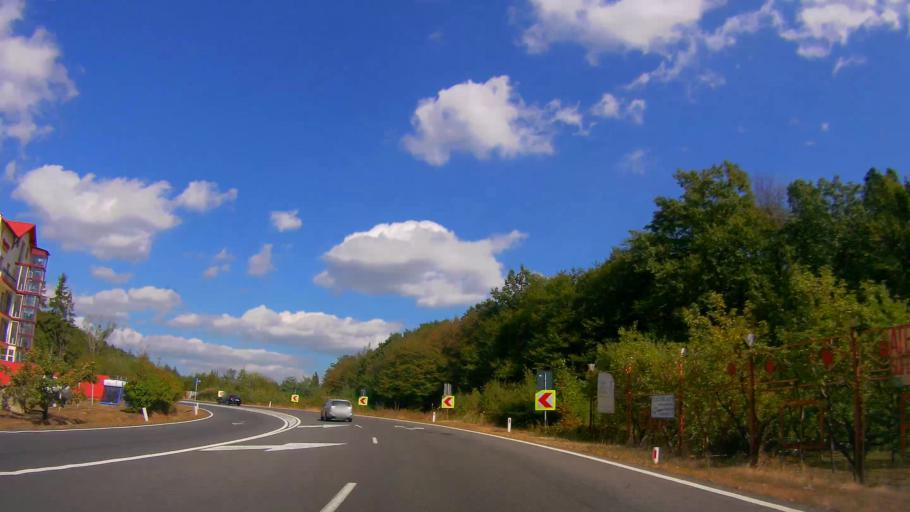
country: RO
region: Salaj
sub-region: Comuna Treznea
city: Treznea
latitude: 47.1456
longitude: 23.1040
